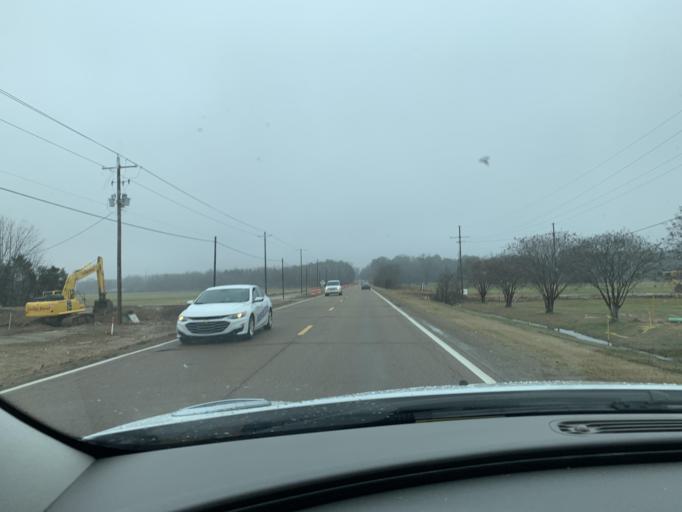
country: US
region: Mississippi
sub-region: De Soto County
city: Hernando
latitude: 34.8678
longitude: -89.9955
